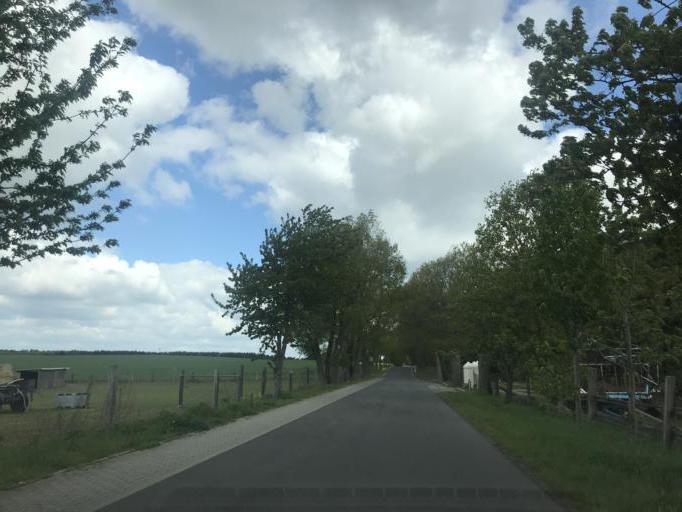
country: DE
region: Brandenburg
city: Gransee
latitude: 52.9026
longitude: 13.1961
